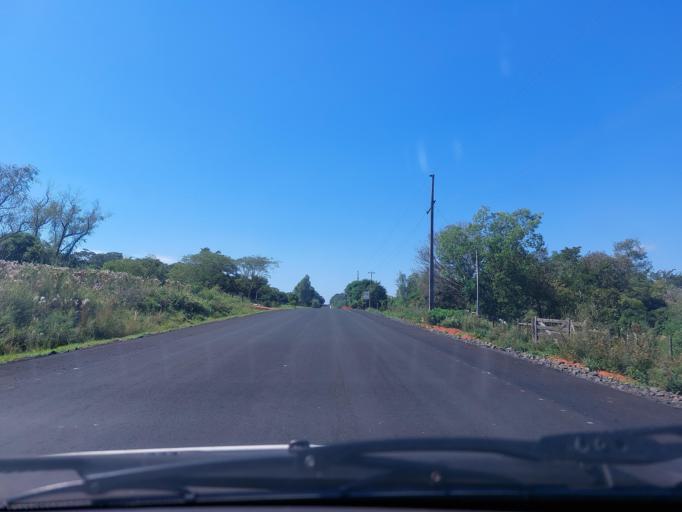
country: PY
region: San Pedro
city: Guayaybi
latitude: -24.5503
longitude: -56.5067
